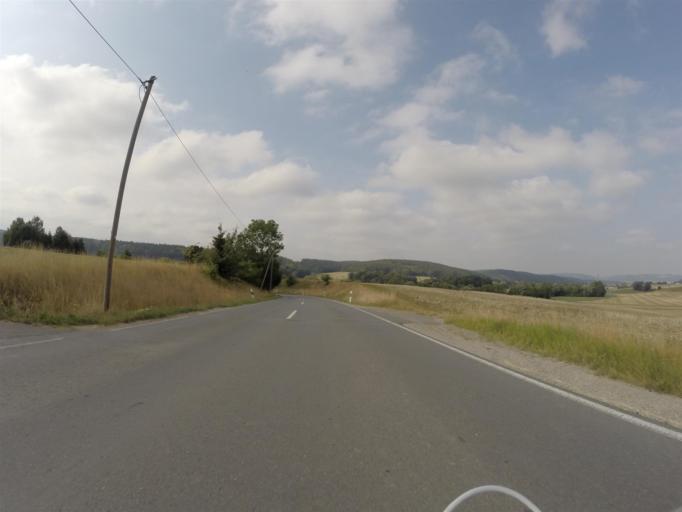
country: DE
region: Thuringia
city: Rausdorf
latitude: 50.8718
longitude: 11.6954
